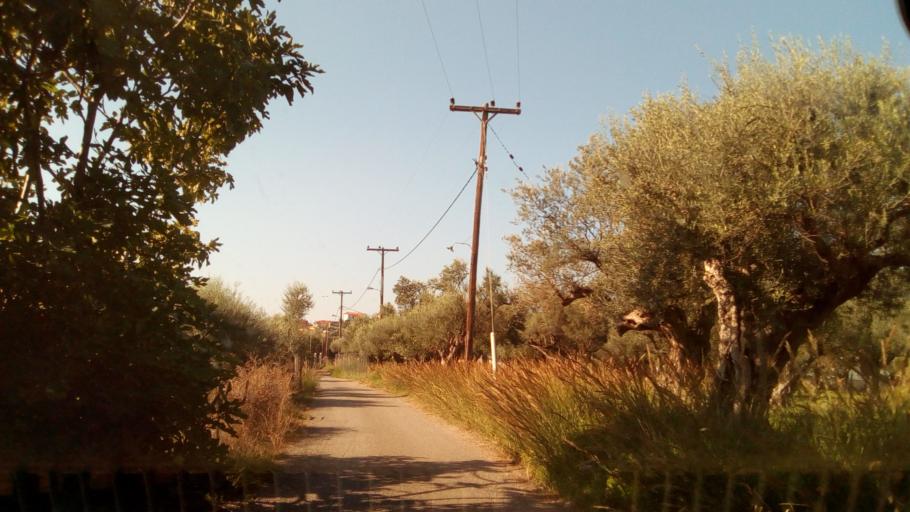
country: GR
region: West Greece
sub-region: Nomos Aitolias kai Akarnanias
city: Nafpaktos
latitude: 38.3839
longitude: 21.8012
